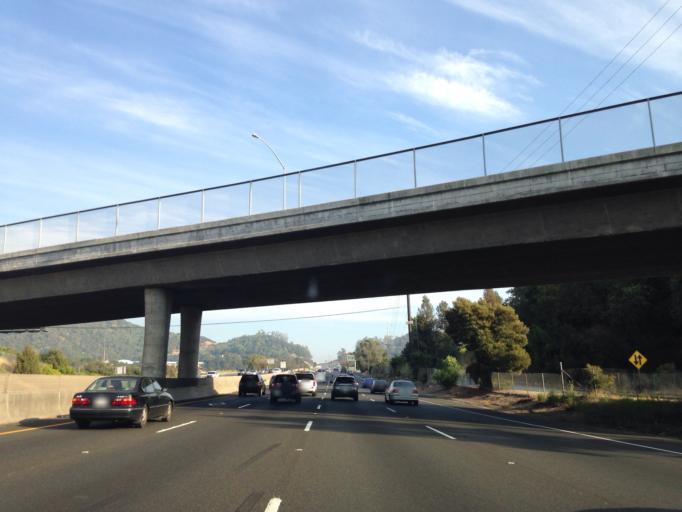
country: US
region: California
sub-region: Marin County
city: Santa Venetia
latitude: 38.0041
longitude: -122.5396
